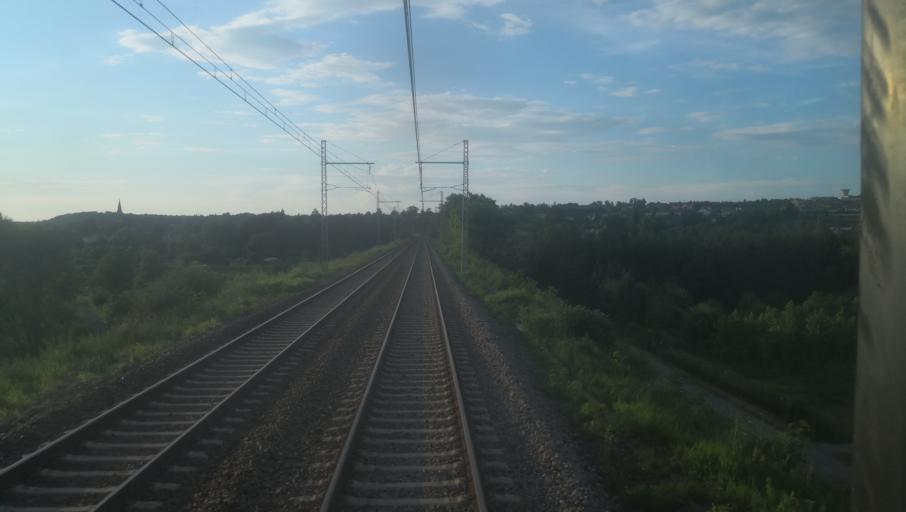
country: FR
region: Centre
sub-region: Departement de l'Indre
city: Argenton-sur-Creuse
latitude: 46.5803
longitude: 1.5256
